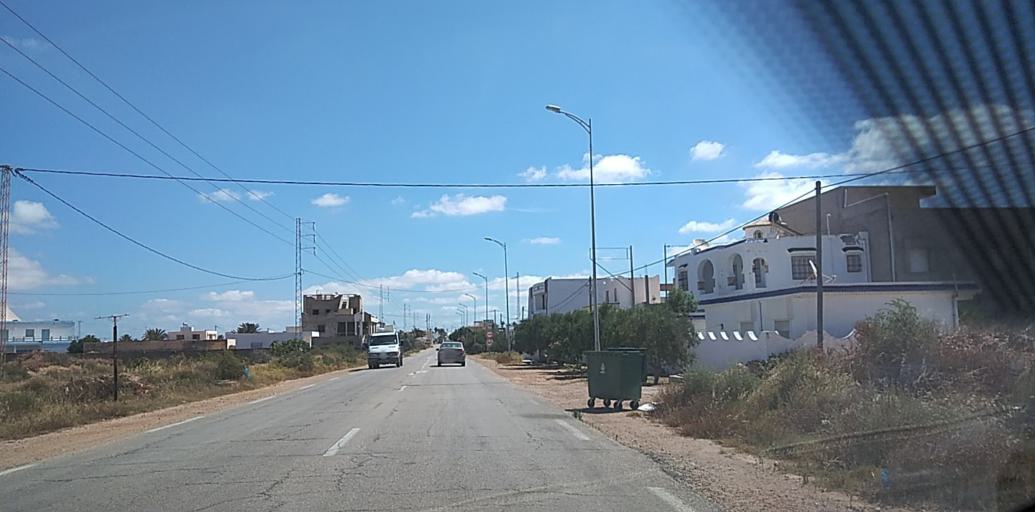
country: TN
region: Safaqis
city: Al Qarmadah
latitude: 34.6693
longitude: 11.1347
